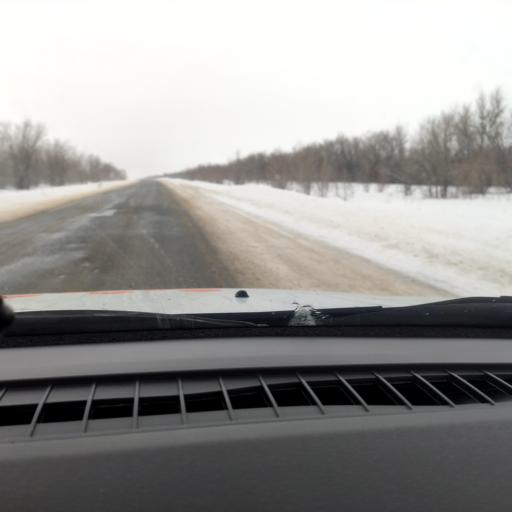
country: RU
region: Samara
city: Mayskoye
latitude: 52.4353
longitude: 50.5503
